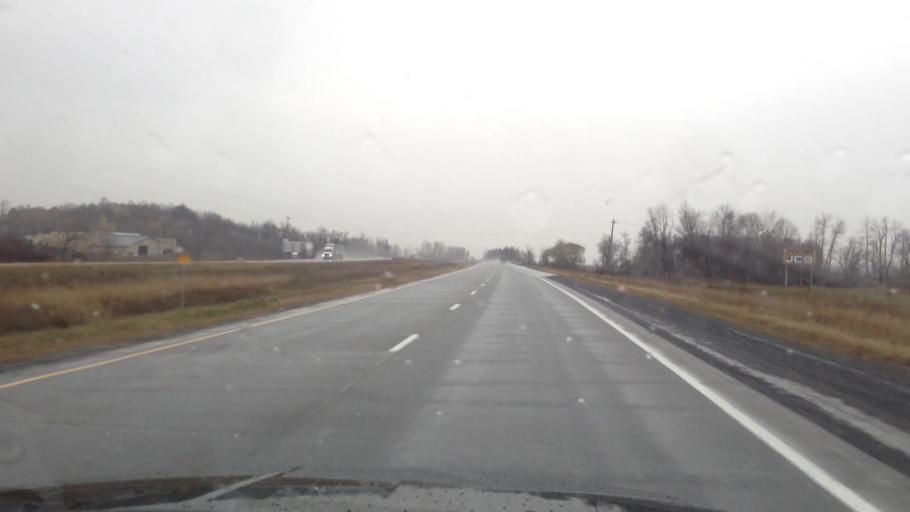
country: CA
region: Ontario
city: Casselman
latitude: 45.3504
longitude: -74.8900
